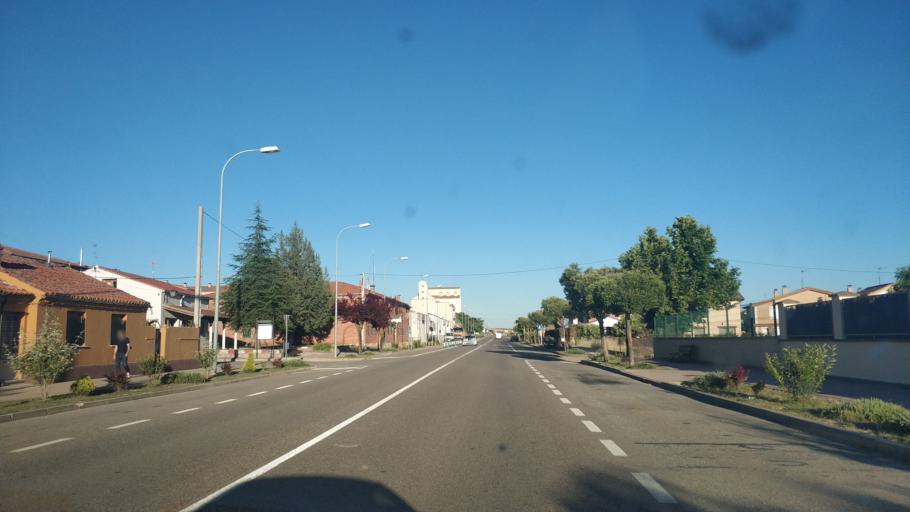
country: ES
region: Castille and Leon
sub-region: Provincia de Soria
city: San Esteban de Gormaz
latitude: 41.5704
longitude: -3.1952
